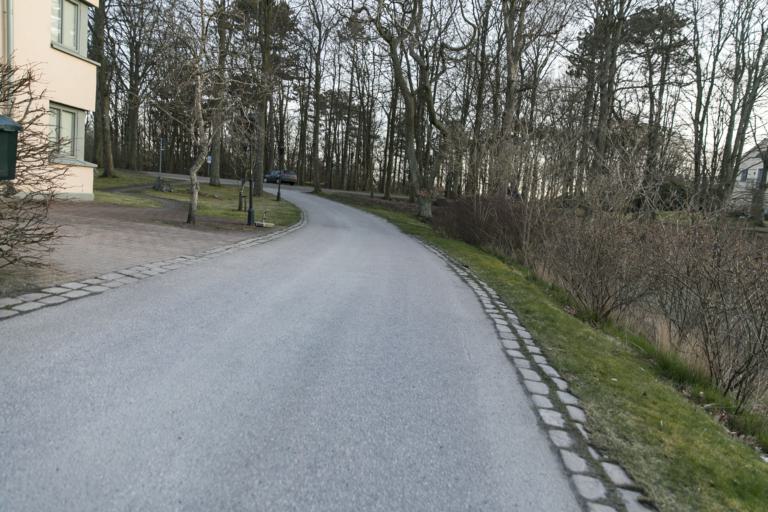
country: SE
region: Halland
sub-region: Varbergs Kommun
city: Varberg
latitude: 57.0869
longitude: 12.2451
